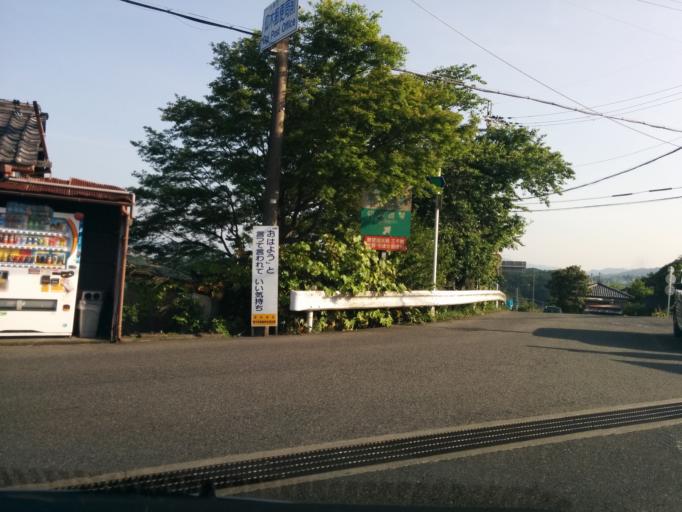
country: JP
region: Shiga Prefecture
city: Kitahama
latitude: 35.1077
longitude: 135.8813
